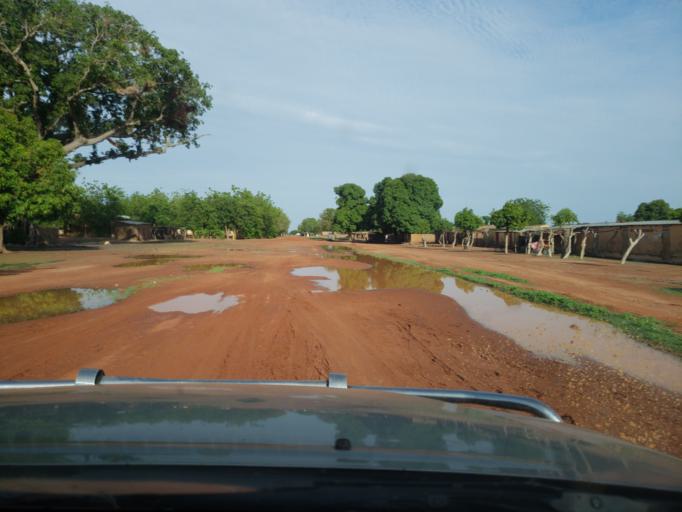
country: ML
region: Sikasso
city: Koutiala
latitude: 12.4228
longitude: -5.6825
